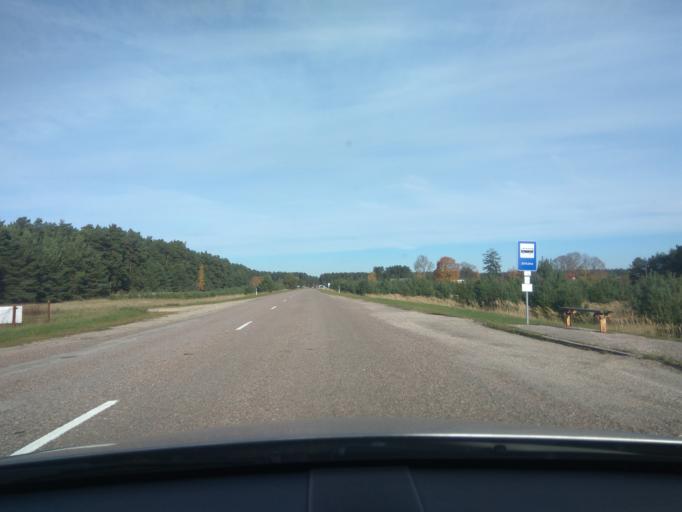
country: LV
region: Alsunga
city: Alsunga
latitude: 57.0076
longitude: 21.3880
